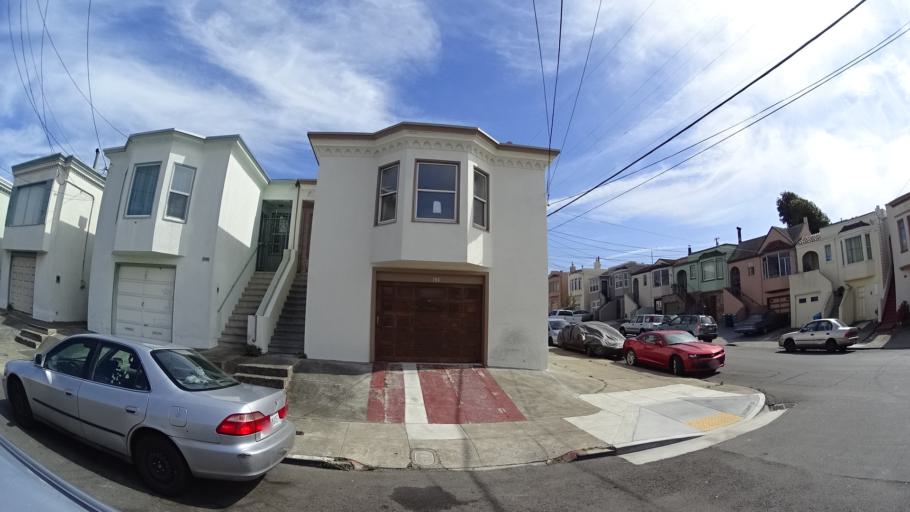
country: US
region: California
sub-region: San Mateo County
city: Daly City
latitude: 37.7146
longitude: -122.4447
